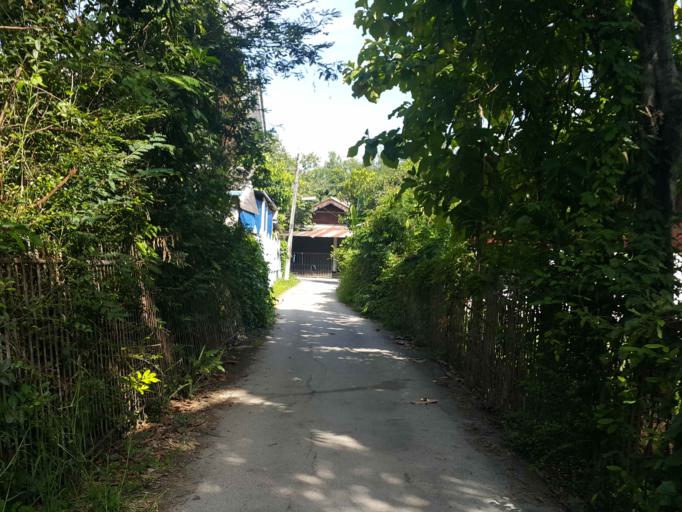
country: TH
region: Chiang Mai
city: San Sai
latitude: 18.8076
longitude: 99.0920
